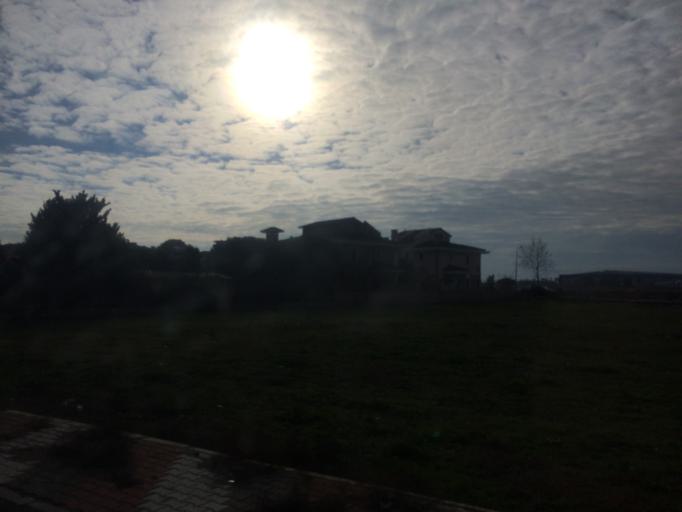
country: TR
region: Izmir
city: Menemen
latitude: 38.5030
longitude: 26.9593
